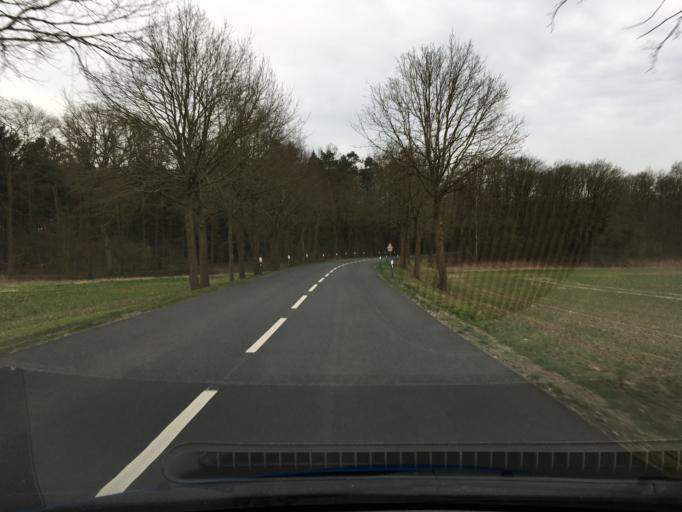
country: DE
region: Lower Saxony
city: Emmendorf
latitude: 53.0282
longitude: 10.6050
